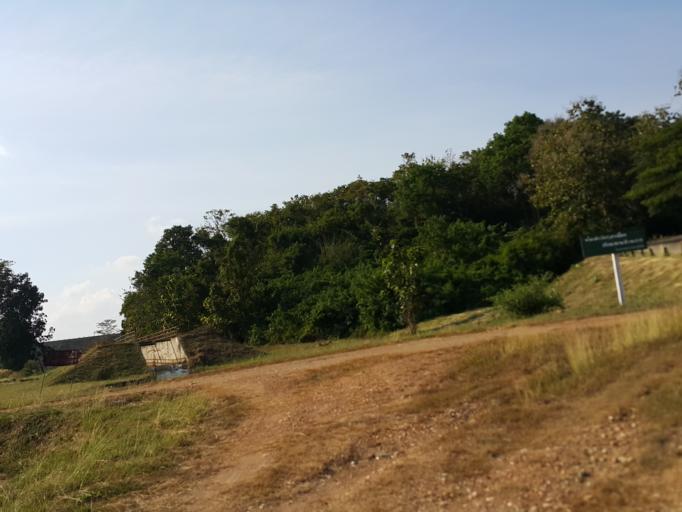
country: TH
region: Sukhothai
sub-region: Amphoe Si Satchanalai
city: Si Satchanalai
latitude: 17.4836
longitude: 99.6319
